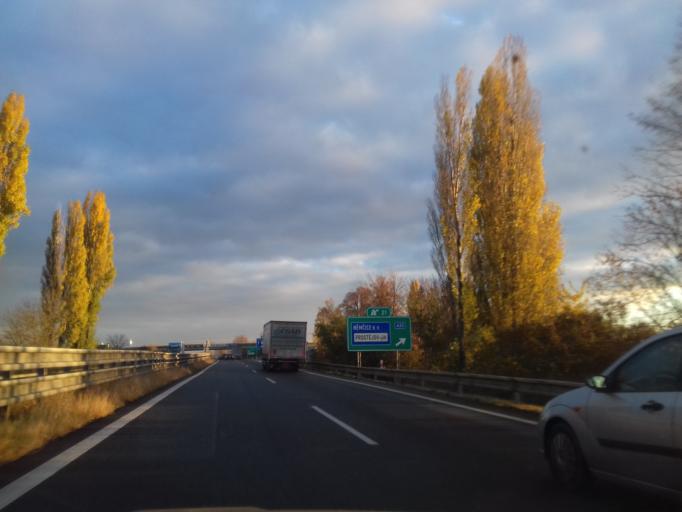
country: CZ
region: Olomoucky
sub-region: Okres Prostejov
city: Prostejov
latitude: 49.4413
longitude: 17.1115
